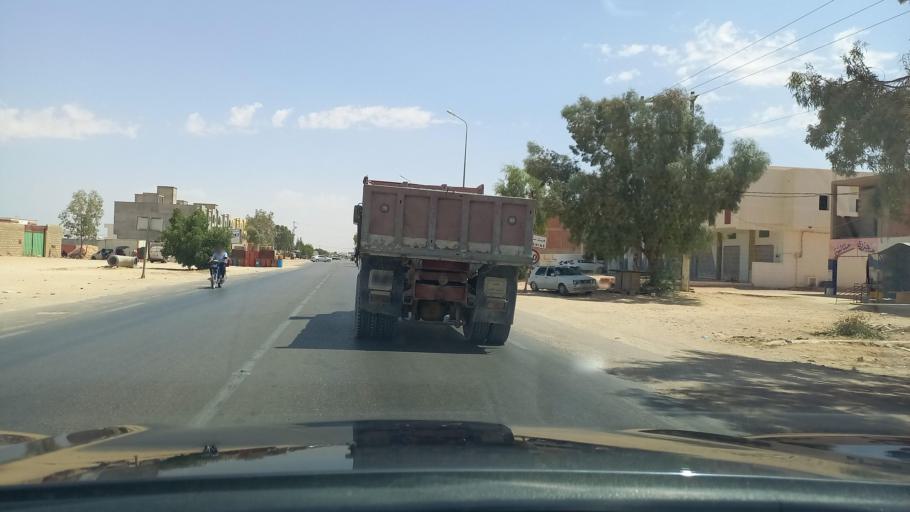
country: TN
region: Madanin
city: Medenine
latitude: 33.3664
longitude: 10.4569
